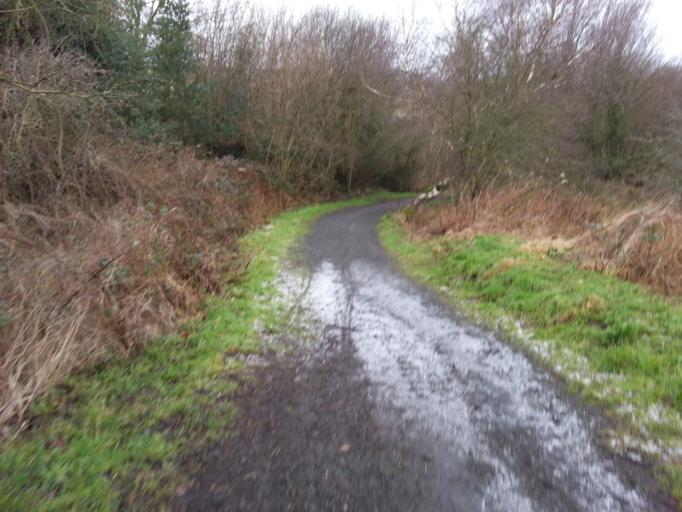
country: GB
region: England
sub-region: County Durham
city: Crook
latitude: 54.7572
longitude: -1.7308
